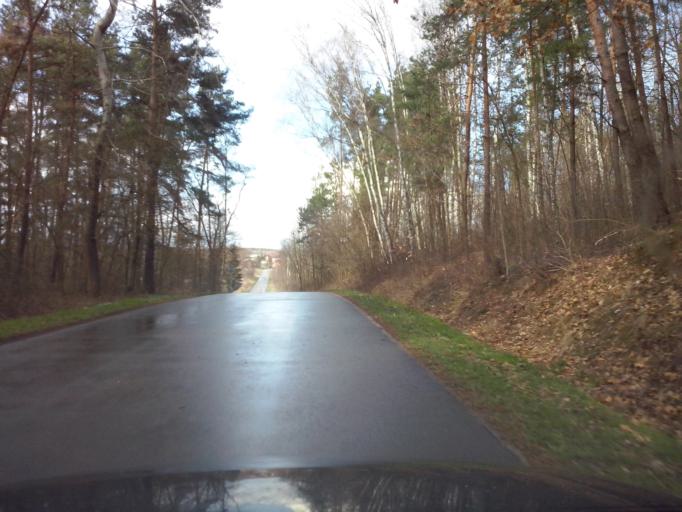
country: PL
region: Subcarpathian Voivodeship
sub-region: Powiat nizanski
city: Bieliny
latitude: 50.4339
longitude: 22.3056
